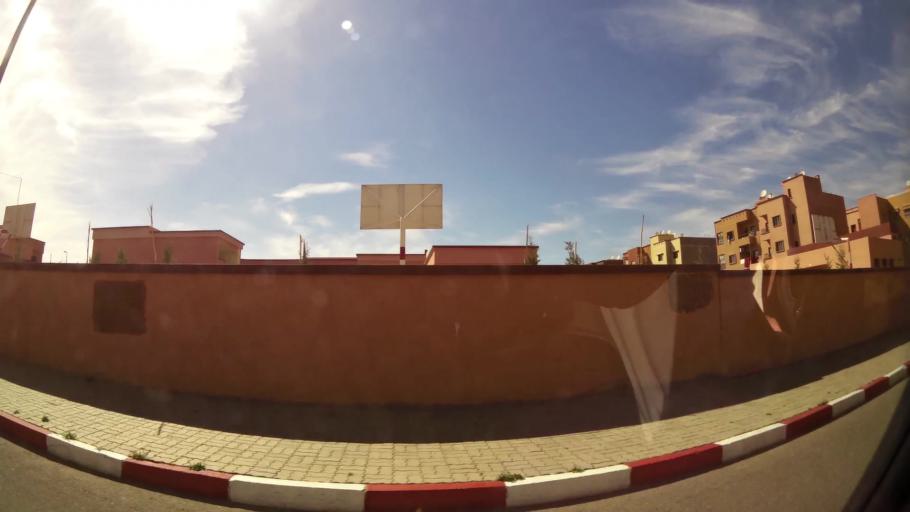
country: MA
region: Marrakech-Tensift-Al Haouz
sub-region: Marrakech
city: Marrakesh
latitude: 31.6703
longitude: -8.0233
